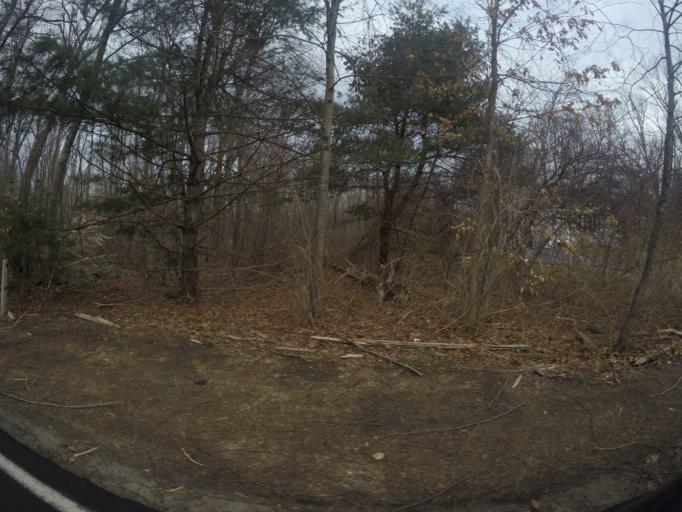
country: US
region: Massachusetts
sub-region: Bristol County
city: Easton
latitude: 42.0514
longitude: -71.1470
